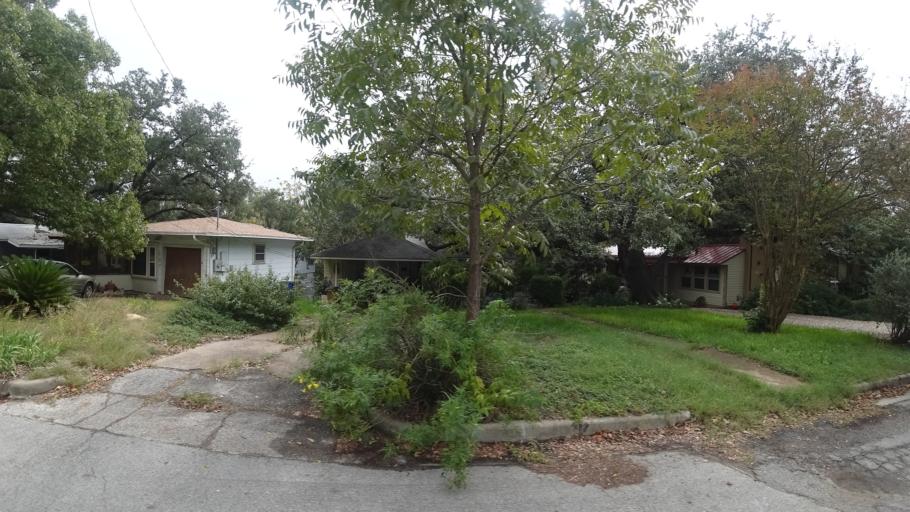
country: US
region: Texas
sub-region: Travis County
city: Austin
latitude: 30.2597
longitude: -97.7613
